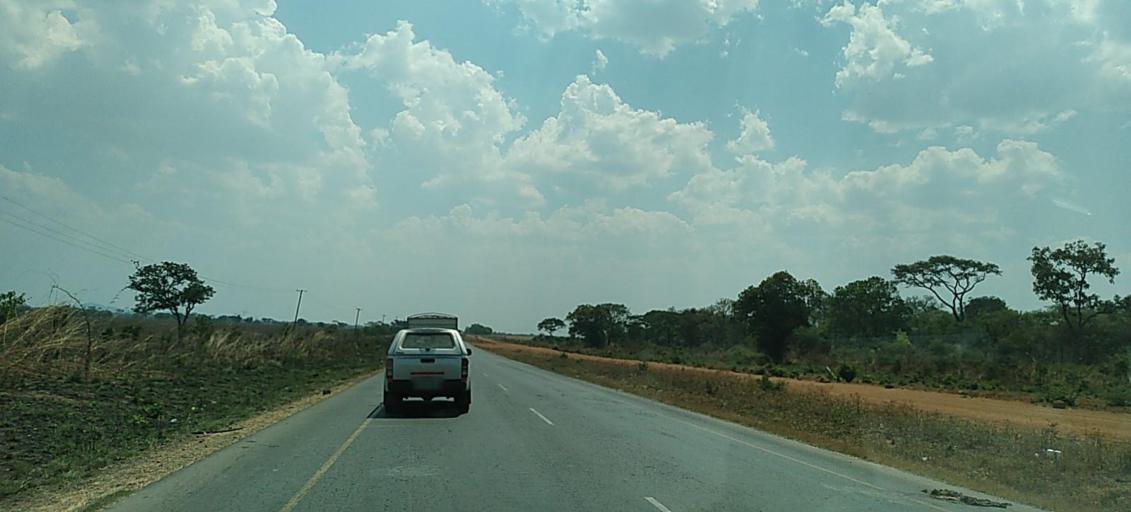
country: ZM
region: Central
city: Kabwe
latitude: -14.5513
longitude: 28.3033
